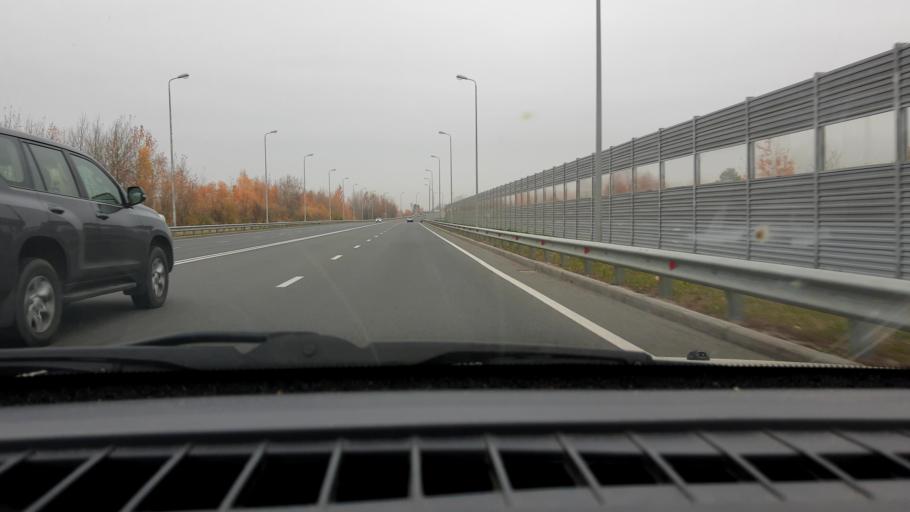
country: RU
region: Nizjnij Novgorod
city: Gorbatovka
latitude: 56.2417
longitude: 43.8071
